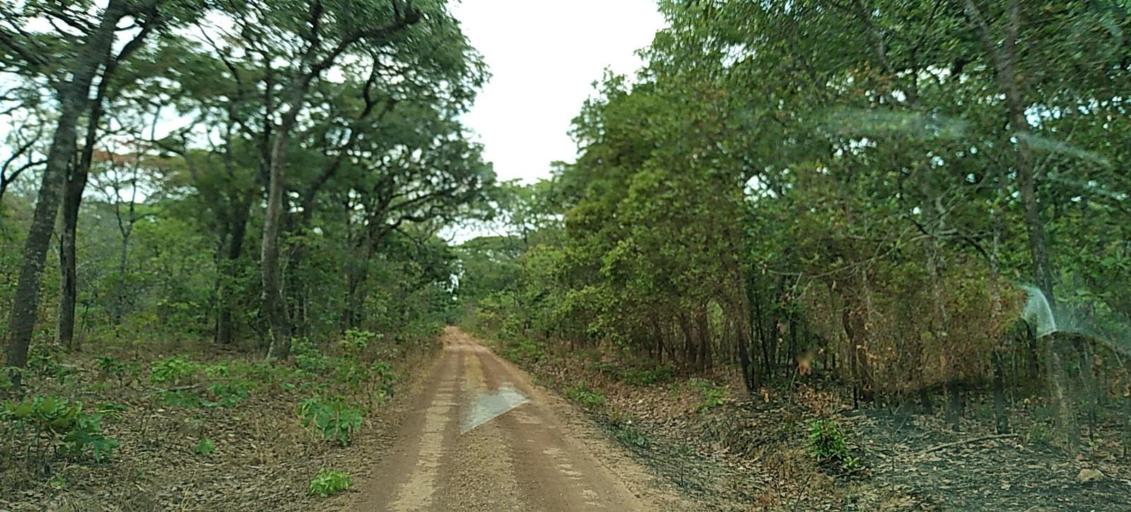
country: ZM
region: Copperbelt
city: Chililabombwe
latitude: -12.4564
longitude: 27.6034
